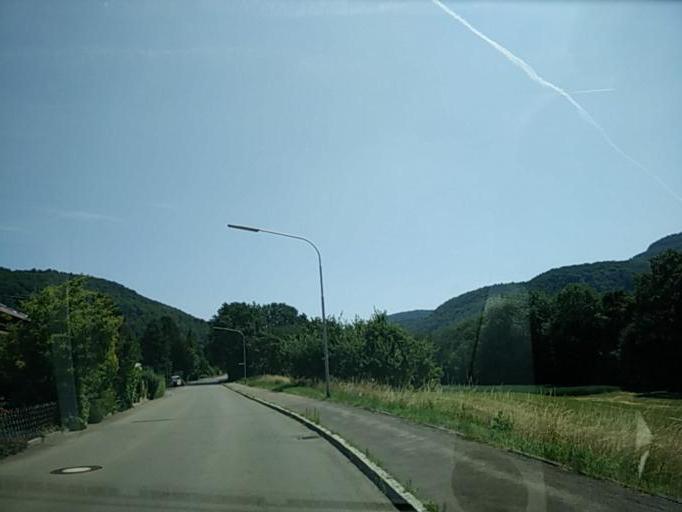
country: DE
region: Baden-Wuerttemberg
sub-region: Tuebingen Region
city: Gomaringen
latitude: 48.4132
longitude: 9.1229
